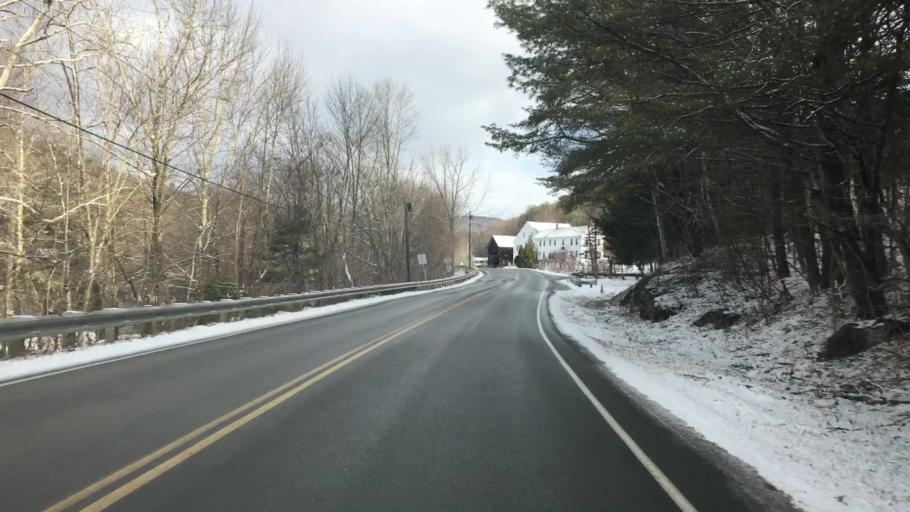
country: US
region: Massachusetts
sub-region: Franklin County
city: Colrain
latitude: 42.7328
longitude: -72.7199
